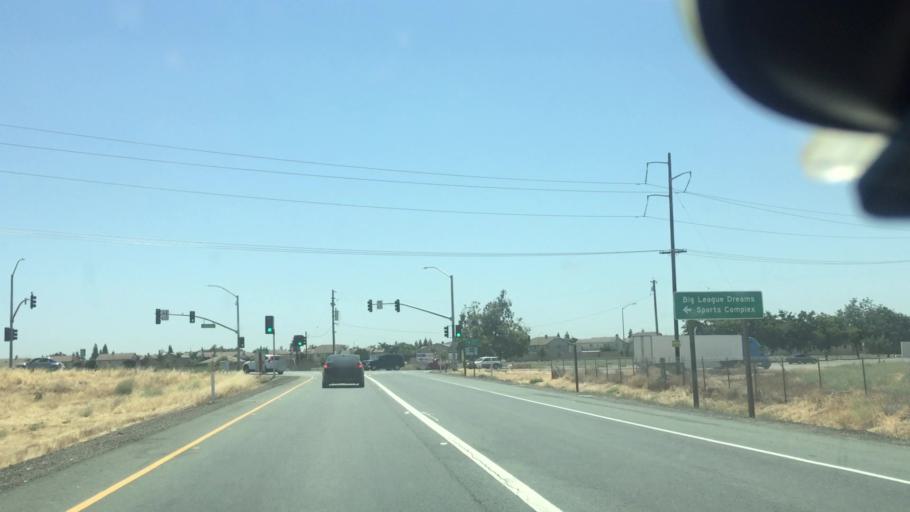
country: US
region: California
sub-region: San Joaquin County
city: Manteca
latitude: 37.7816
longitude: -121.2531
